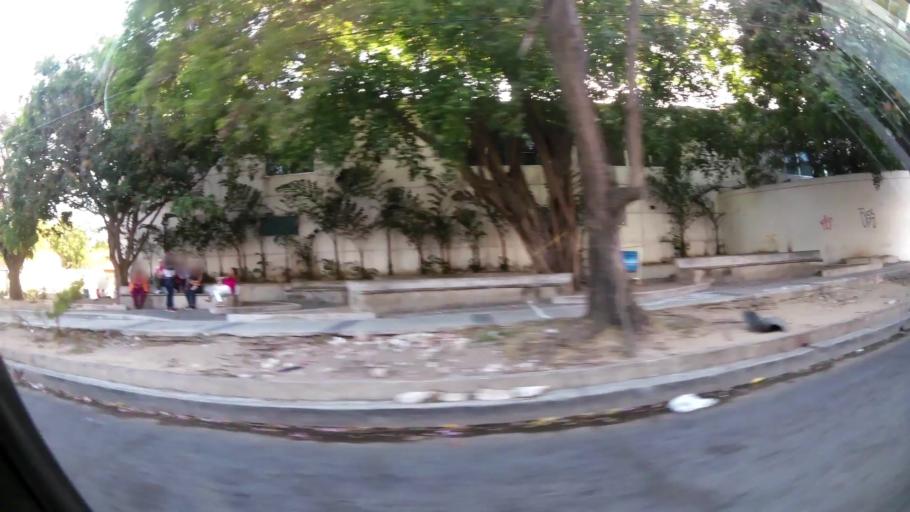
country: CO
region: Atlantico
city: Barranquilla
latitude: 10.9656
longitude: -74.7974
